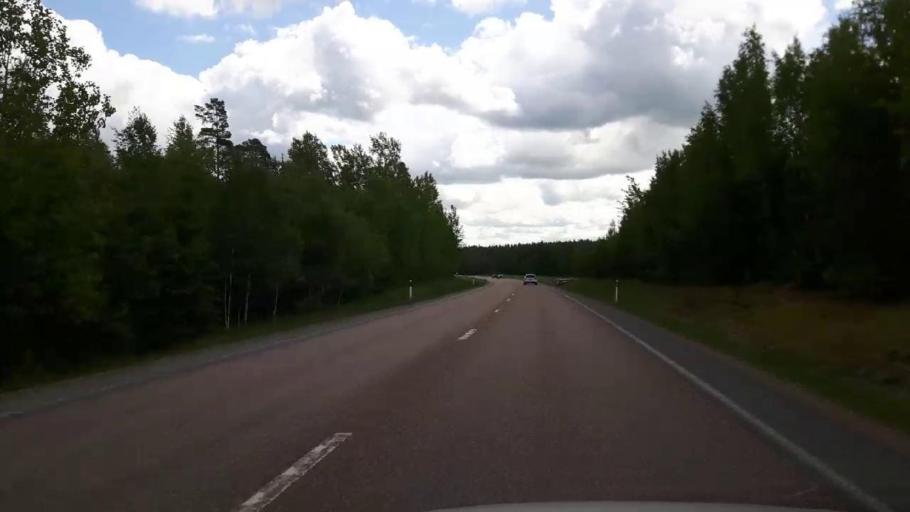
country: SE
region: Dalarna
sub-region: Faluns Kommun
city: Falun
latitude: 60.5036
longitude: 15.7418
